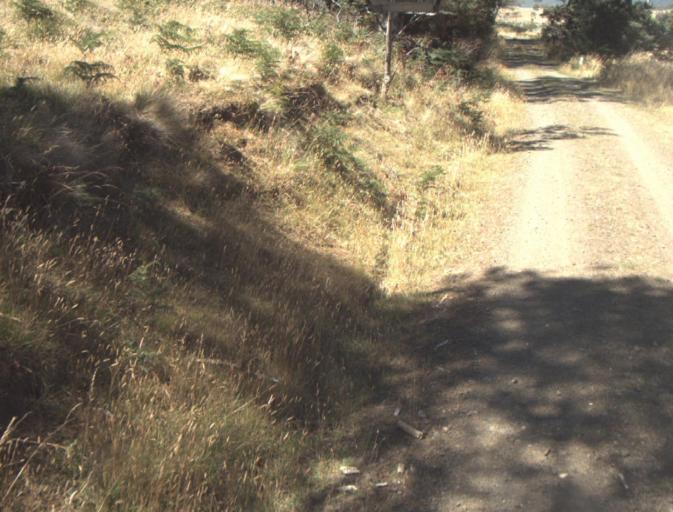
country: AU
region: Tasmania
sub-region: Dorset
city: Scottsdale
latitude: -41.3514
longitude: 147.4417
